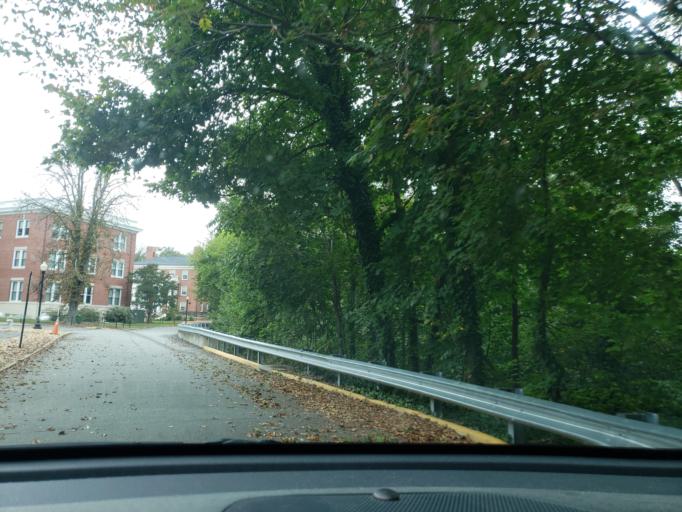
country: US
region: Virginia
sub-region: City of Fredericksburg
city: Fredericksburg
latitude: 38.3040
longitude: -77.4745
